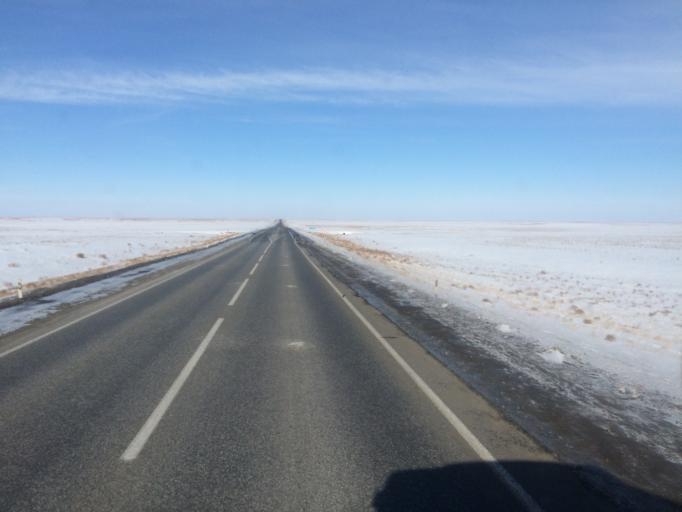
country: KZ
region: Qyzylorda
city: Sekseuil
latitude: 47.5704
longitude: 61.5119
